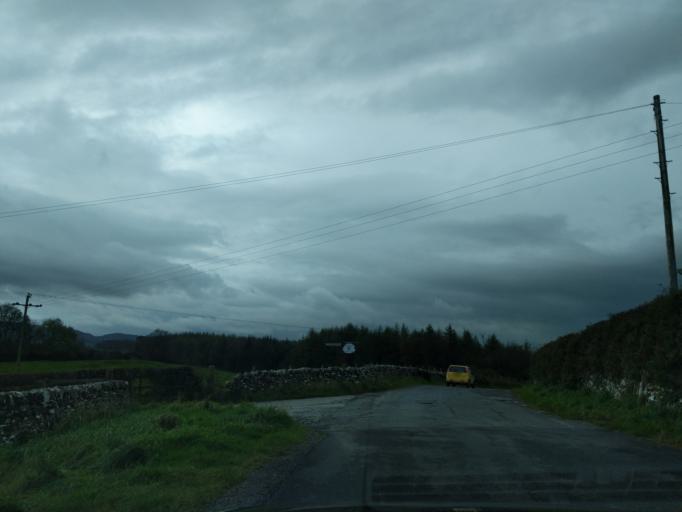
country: GB
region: Scotland
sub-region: Dumfries and Galloway
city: Castle Douglas
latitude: 54.9215
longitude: -3.9562
